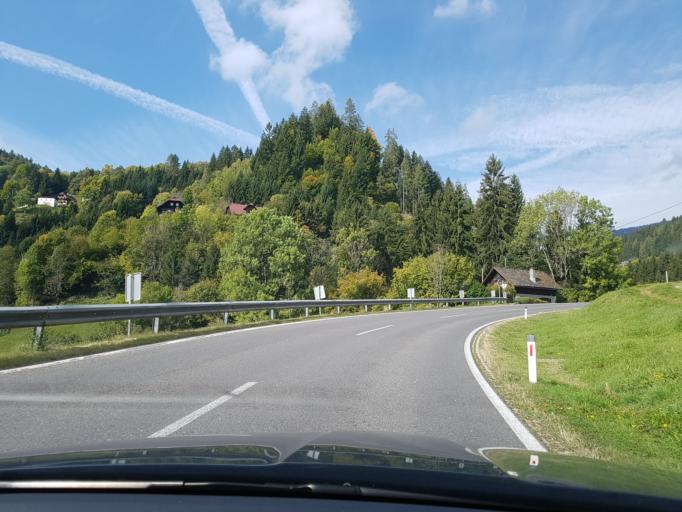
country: AT
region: Carinthia
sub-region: Politischer Bezirk Feldkirchen
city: Himmelberg
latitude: 46.7589
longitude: 14.0242
